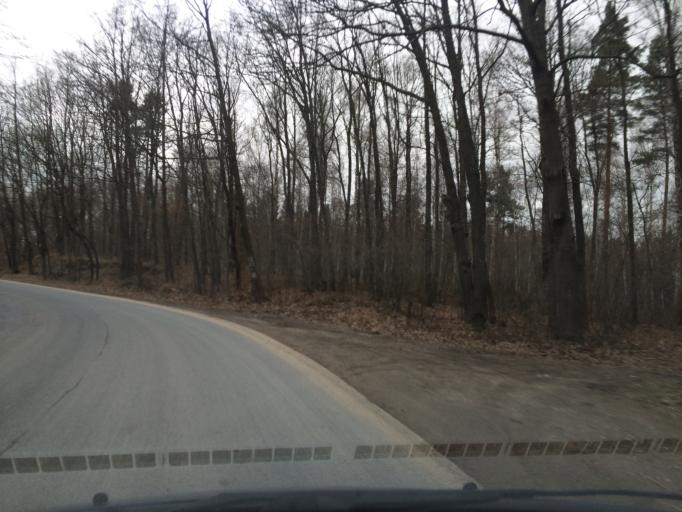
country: PL
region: Lower Silesian Voivodeship
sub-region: Powiat lwowecki
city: Lwowek Slaski
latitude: 51.1212
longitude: 15.5154
